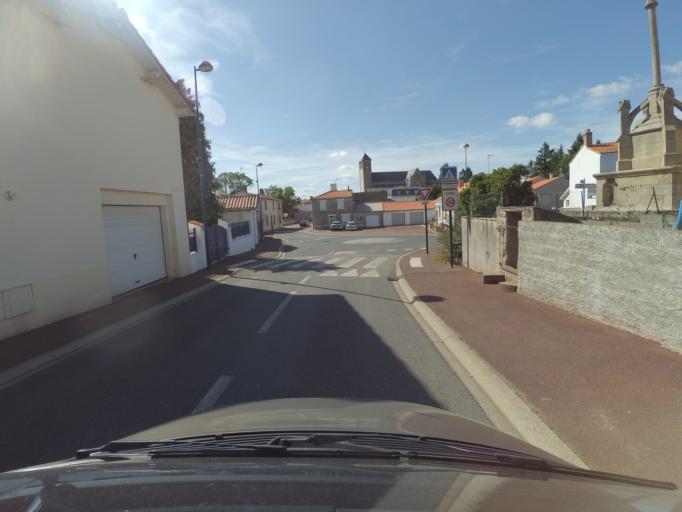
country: FR
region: Pays de la Loire
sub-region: Departement de la Loire-Atlantique
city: Le Bignon
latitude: 47.0976
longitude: -1.4873
